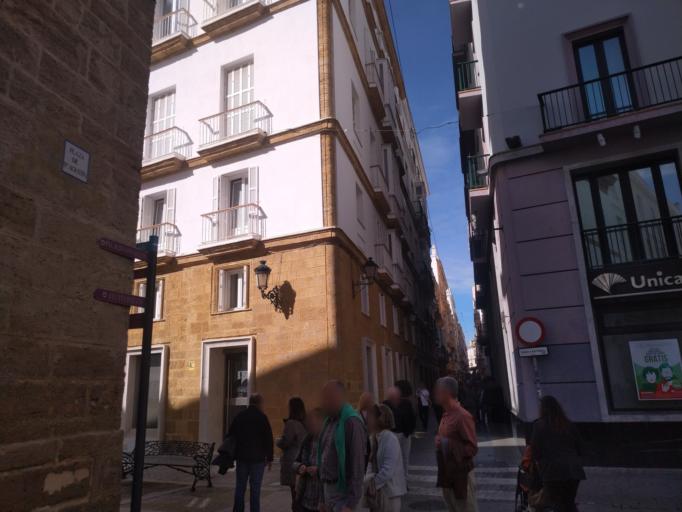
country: ES
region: Andalusia
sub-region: Provincia de Cadiz
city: Cadiz
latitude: 36.5324
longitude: -6.2940
